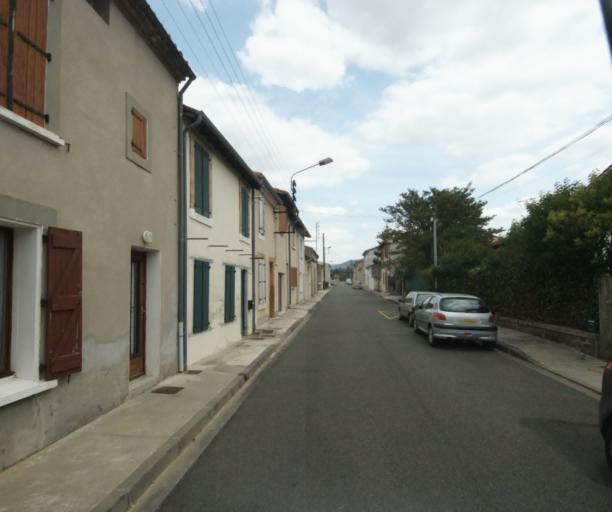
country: FR
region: Midi-Pyrenees
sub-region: Departement de la Haute-Garonne
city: Revel
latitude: 43.4558
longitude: 2.0056
